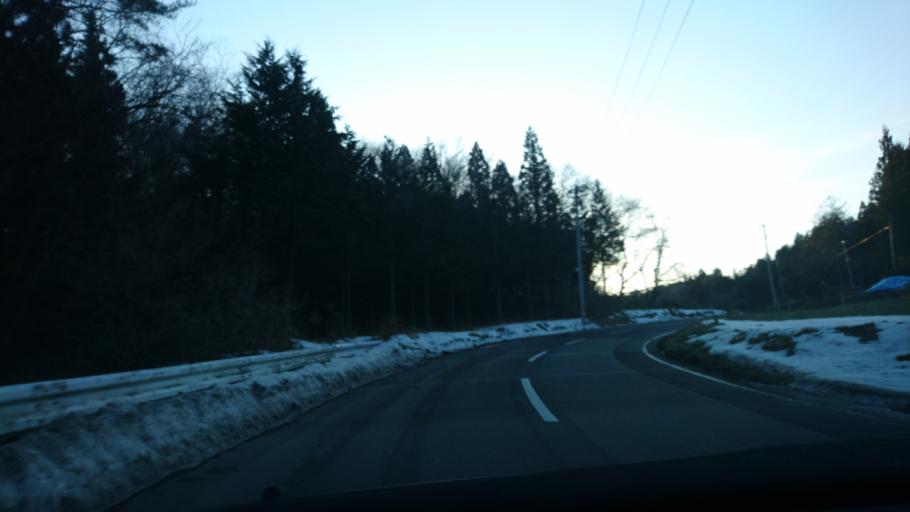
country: JP
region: Iwate
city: Mizusawa
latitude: 39.0386
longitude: 141.3236
